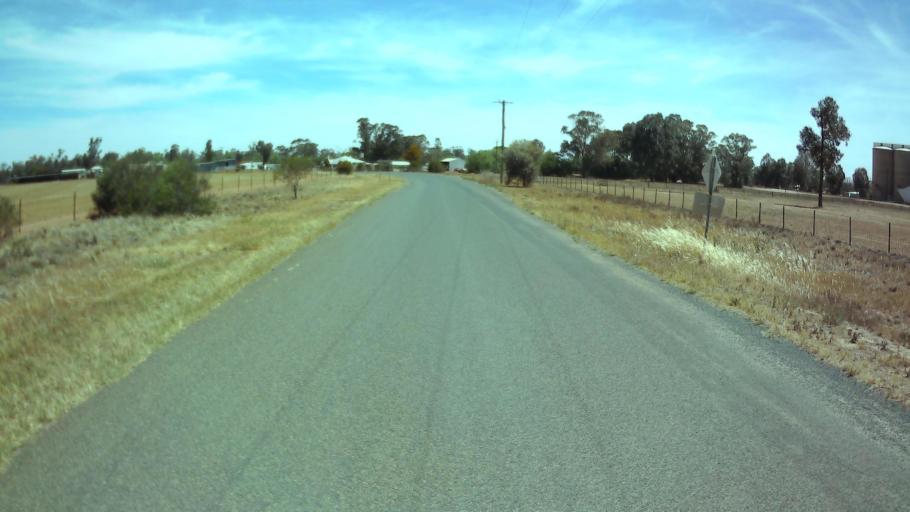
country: AU
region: New South Wales
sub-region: Weddin
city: Grenfell
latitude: -33.8380
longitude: 147.7456
